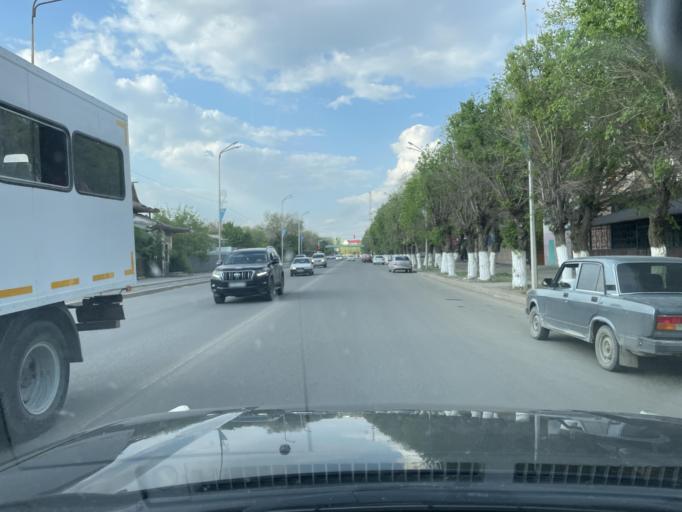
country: KZ
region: Qaraghandy
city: Zhezqazghan
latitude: 47.7901
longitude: 67.7105
